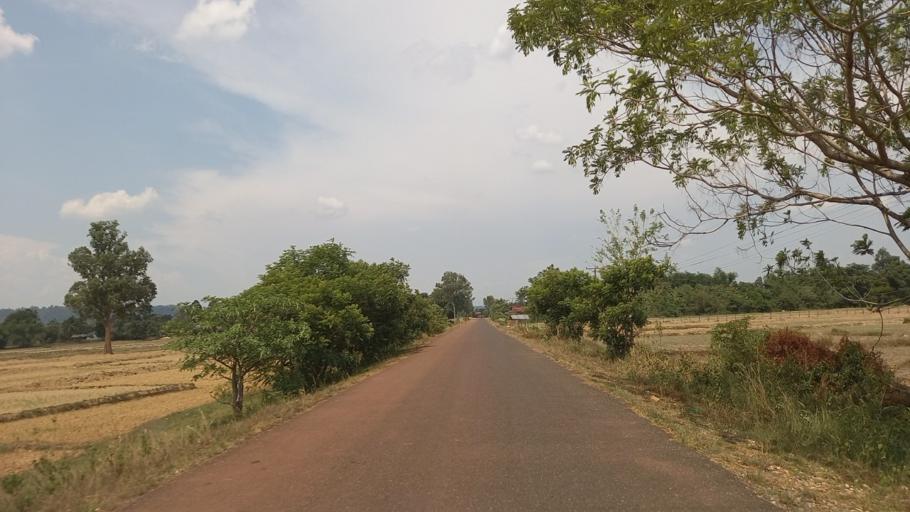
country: LA
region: Bolikhamxai
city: Muang Pakxan
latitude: 18.4294
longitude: 103.7353
